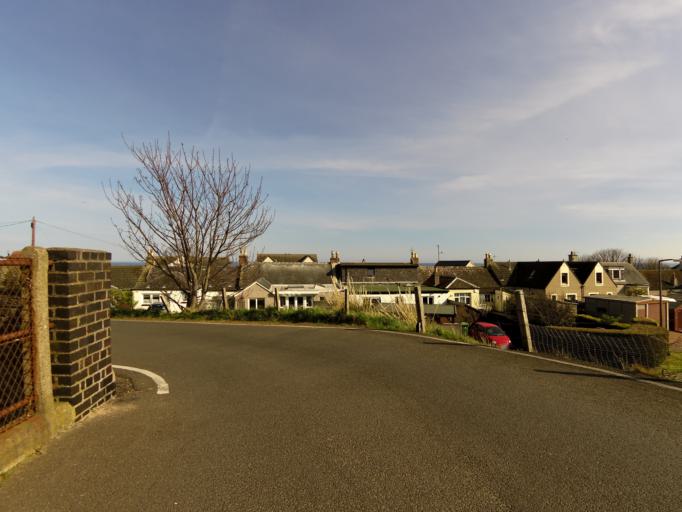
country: GB
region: Scotland
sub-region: Angus
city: Carnoustie
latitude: 56.5029
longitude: -2.6970
